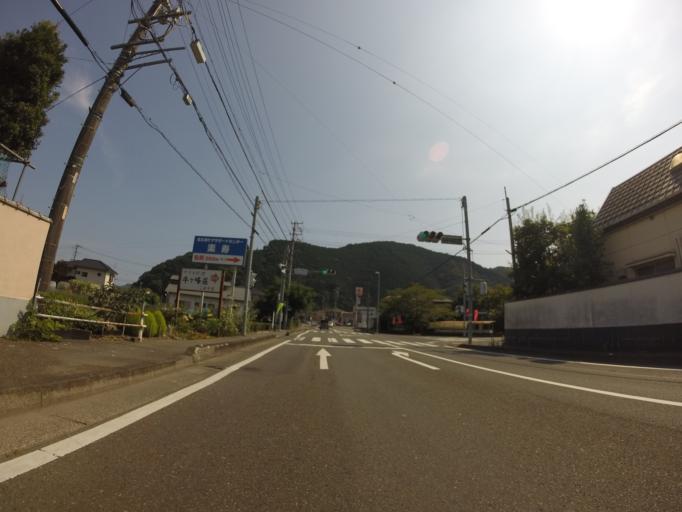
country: JP
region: Shizuoka
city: Shizuoka-shi
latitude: 35.0443
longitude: 138.3658
